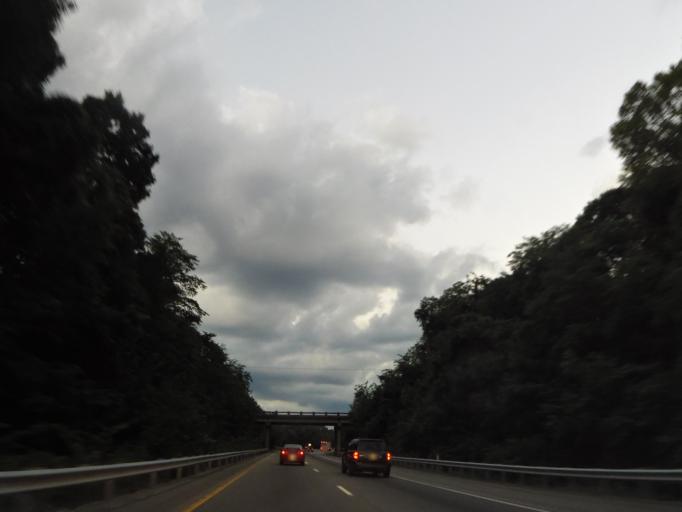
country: US
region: Tennessee
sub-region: Putnam County
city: Algood
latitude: 36.1431
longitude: -85.3755
